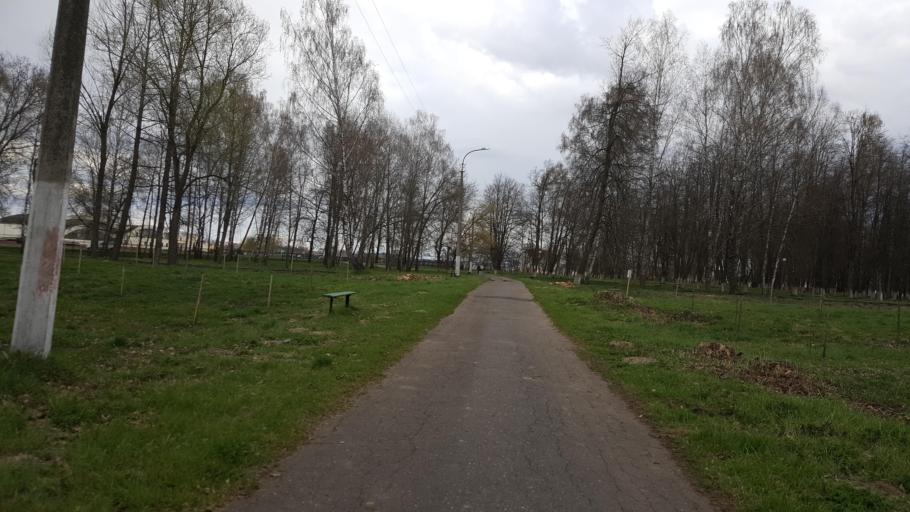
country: BY
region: Brest
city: Kamyanyets
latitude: 52.4004
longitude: 23.8076
